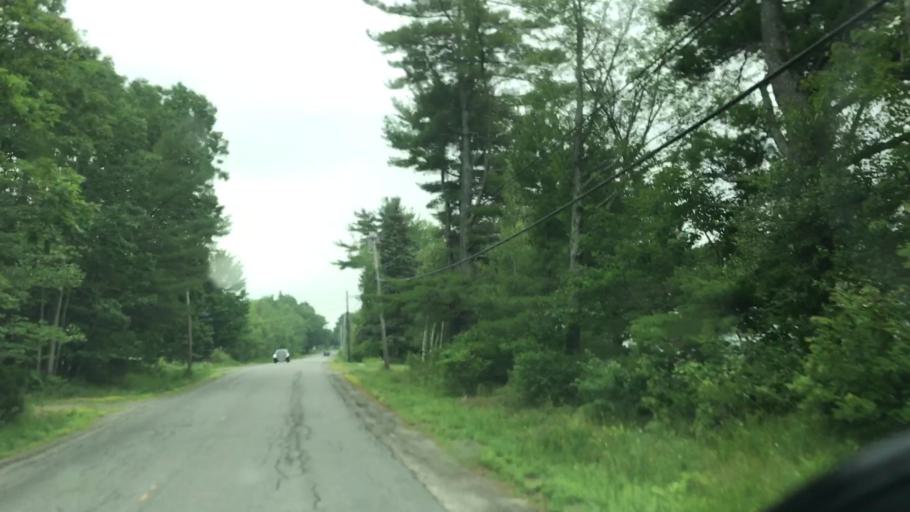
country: US
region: Maine
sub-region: Penobscot County
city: Orono
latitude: 44.8830
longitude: -68.7093
